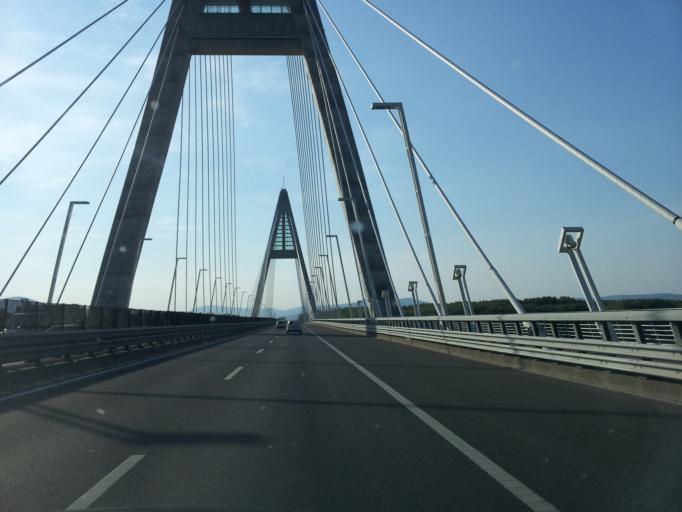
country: HU
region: Budapest
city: Budapest IV. keruelet
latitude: 47.6062
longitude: 19.0949
